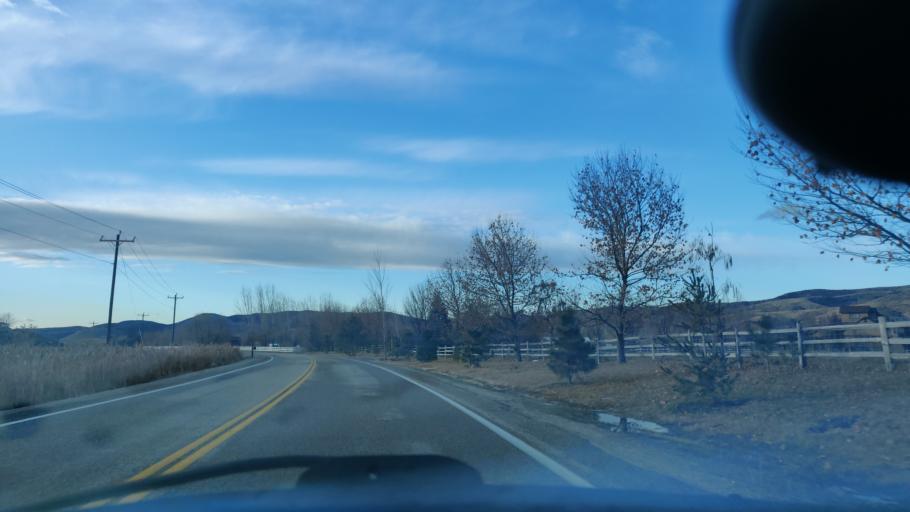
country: US
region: Idaho
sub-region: Ada County
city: Eagle
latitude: 43.7289
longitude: -116.2621
